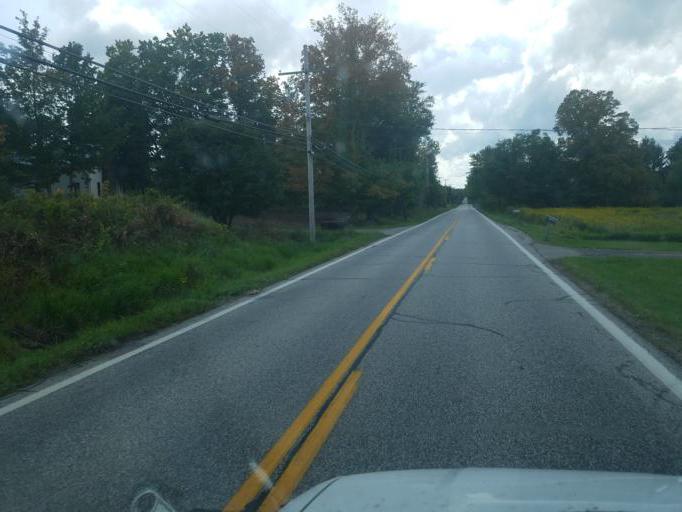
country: US
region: Ohio
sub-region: Geauga County
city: Burton
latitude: 41.4429
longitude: -81.1365
